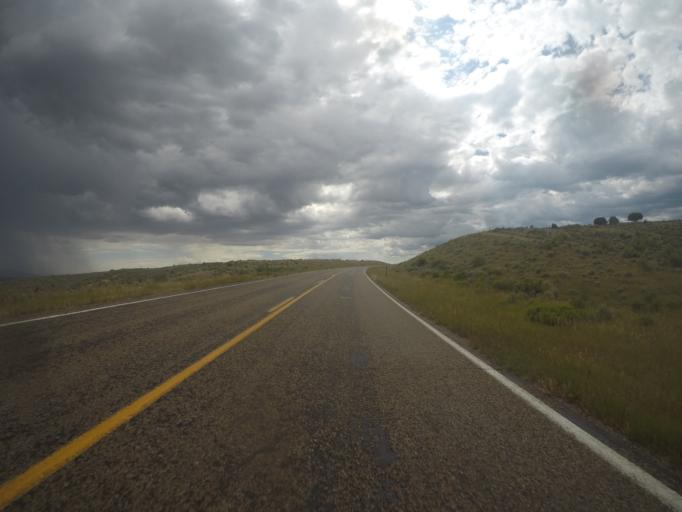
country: US
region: Utah
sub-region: Daggett County
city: Manila
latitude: 41.0276
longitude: -109.8737
